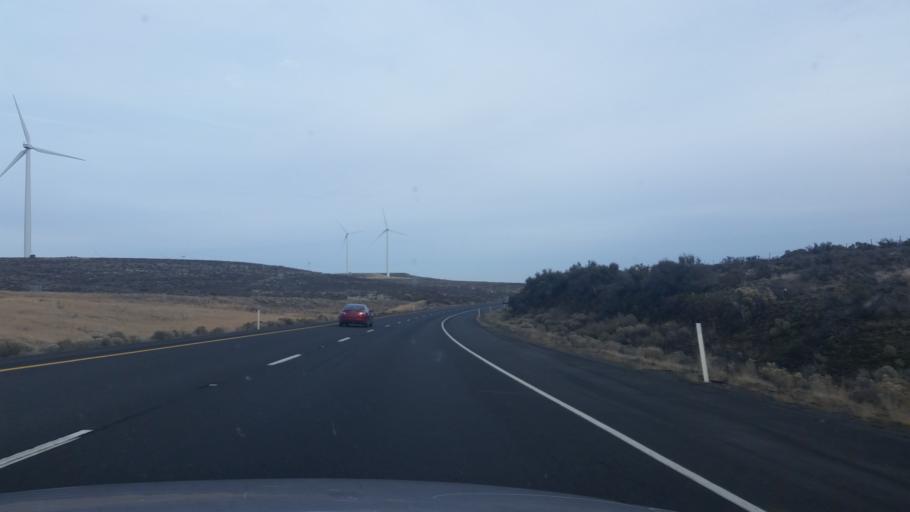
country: US
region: Washington
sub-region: Kittitas County
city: Kittitas
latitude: 46.9449
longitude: -120.1947
